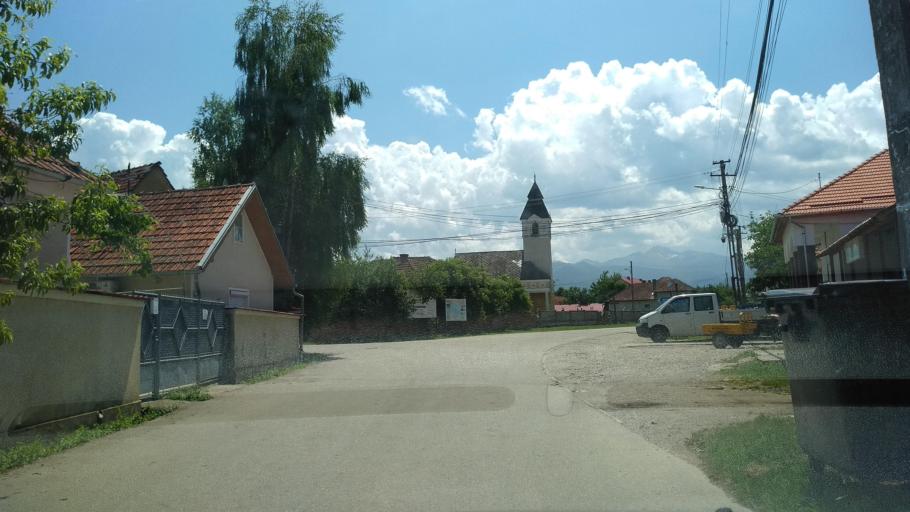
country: RO
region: Hunedoara
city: Densus
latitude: 45.5492
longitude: 22.8235
